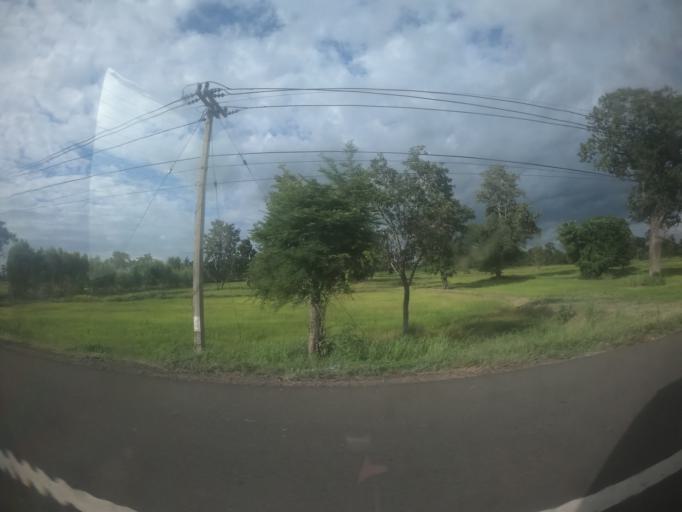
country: TH
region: Surin
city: Prasat
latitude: 14.5818
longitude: 103.4759
